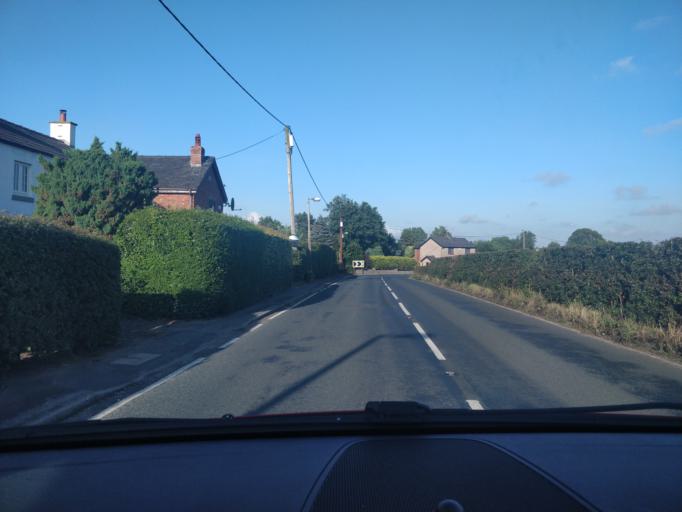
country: GB
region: England
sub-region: Lancashire
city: Tarleton
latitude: 53.6447
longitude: -2.8577
